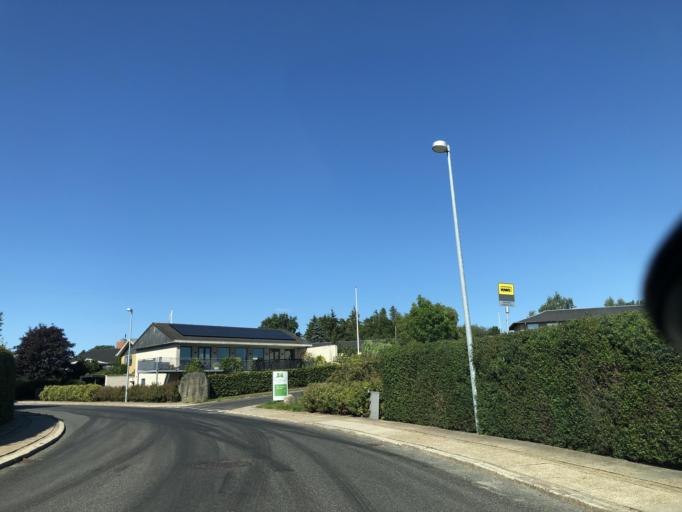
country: DK
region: North Denmark
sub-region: Mariagerfjord Kommune
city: Hobro
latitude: 56.6444
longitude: 9.8052
